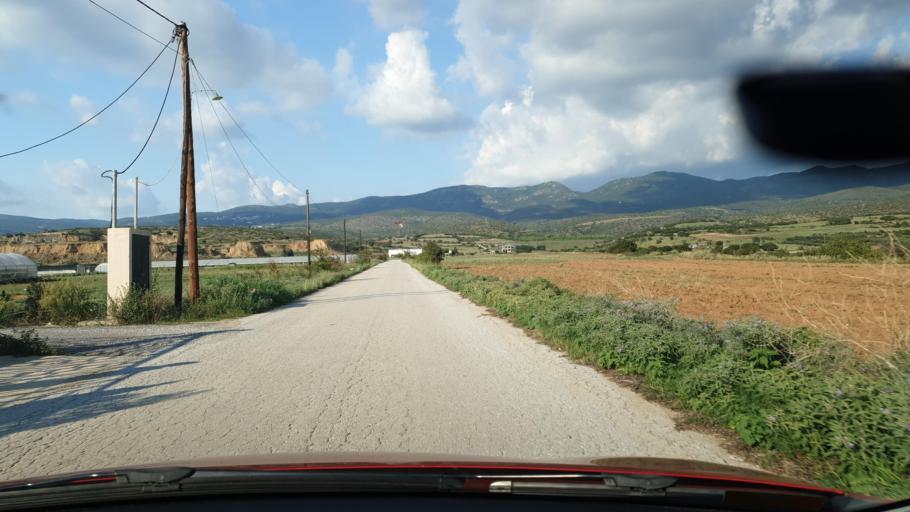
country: GR
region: Central Macedonia
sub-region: Nomos Thessalonikis
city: Vasilika
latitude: 40.4968
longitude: 23.1411
